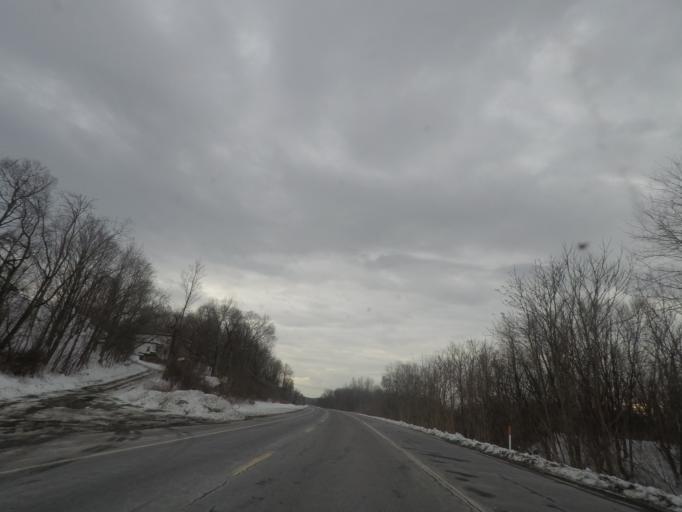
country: US
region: New York
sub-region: Rensselaer County
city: Hampton Manor
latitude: 42.6062
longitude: -73.7475
